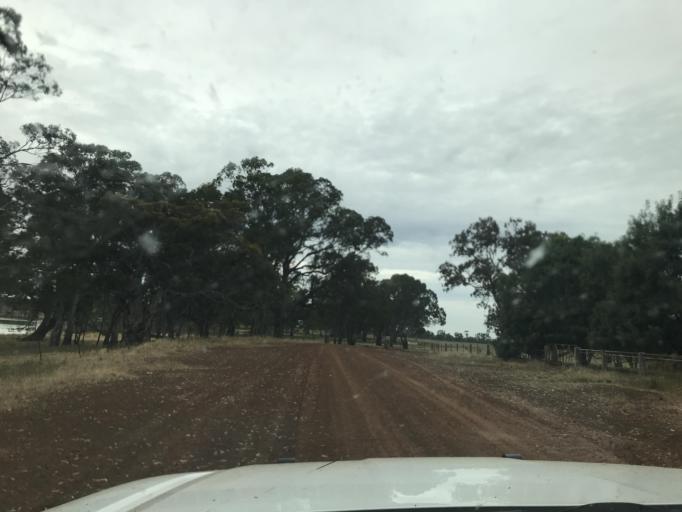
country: AU
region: Victoria
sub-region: Horsham
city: Horsham
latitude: -37.0790
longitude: 141.6667
